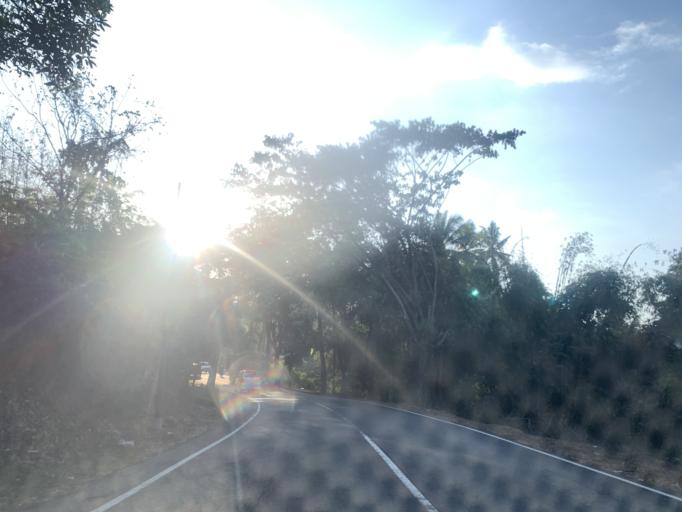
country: ID
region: Bali
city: Angkahgede
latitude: -8.4844
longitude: 114.9484
